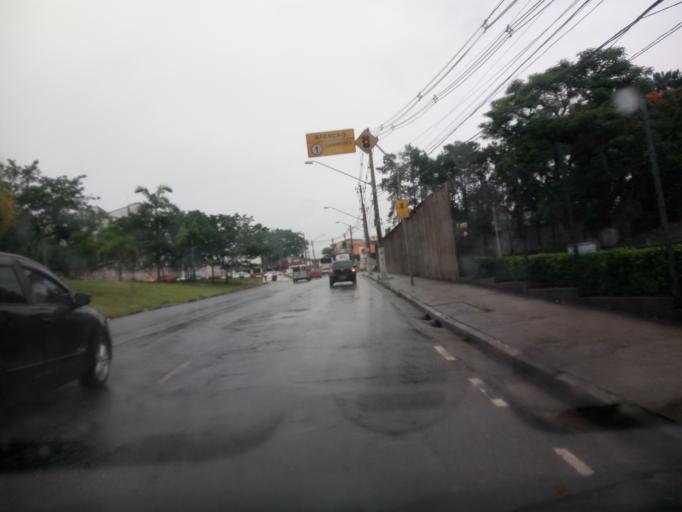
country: BR
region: Sao Paulo
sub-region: Sao Bernardo Do Campo
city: Sao Bernardo do Campo
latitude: -23.7522
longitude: -46.5731
